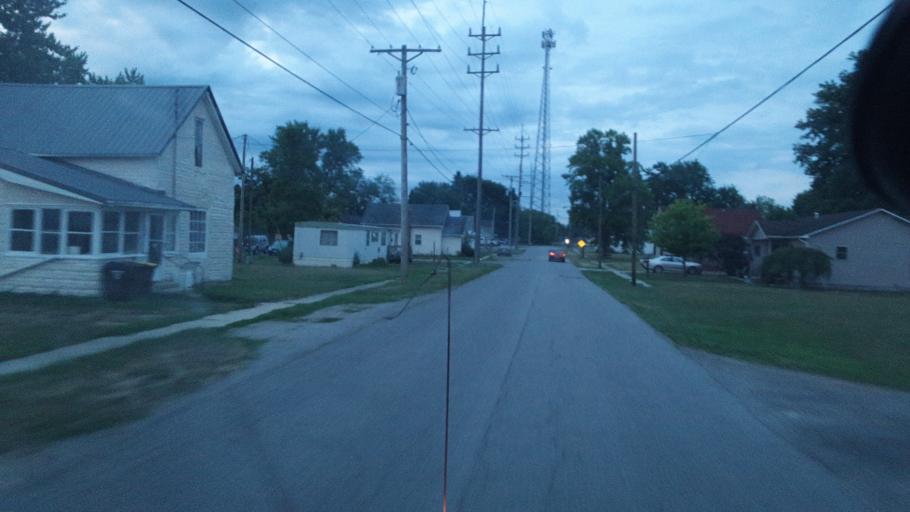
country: US
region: Ohio
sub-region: Defiance County
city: Hicksville
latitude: 41.2983
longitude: -84.7657
